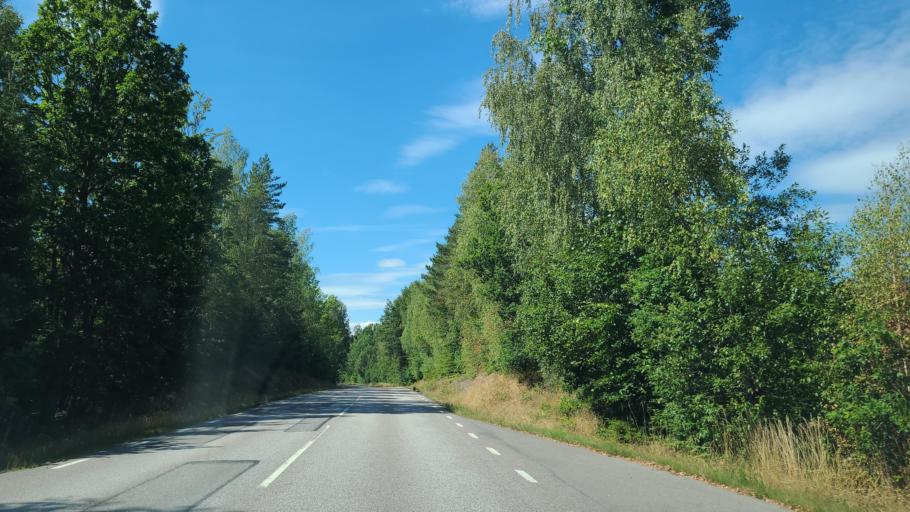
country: SE
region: Kalmar
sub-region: Emmaboda Kommun
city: Emmaboda
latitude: 56.5506
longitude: 15.7014
